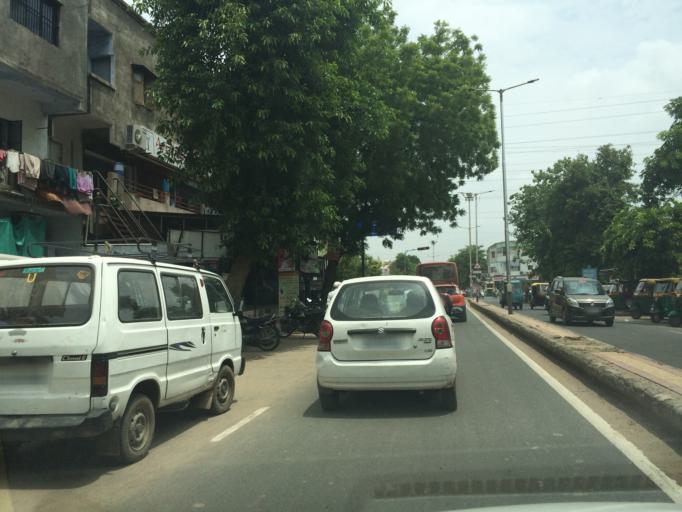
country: IN
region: Gujarat
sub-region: Ahmadabad
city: Ahmedabad
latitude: 23.0685
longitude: 72.5665
